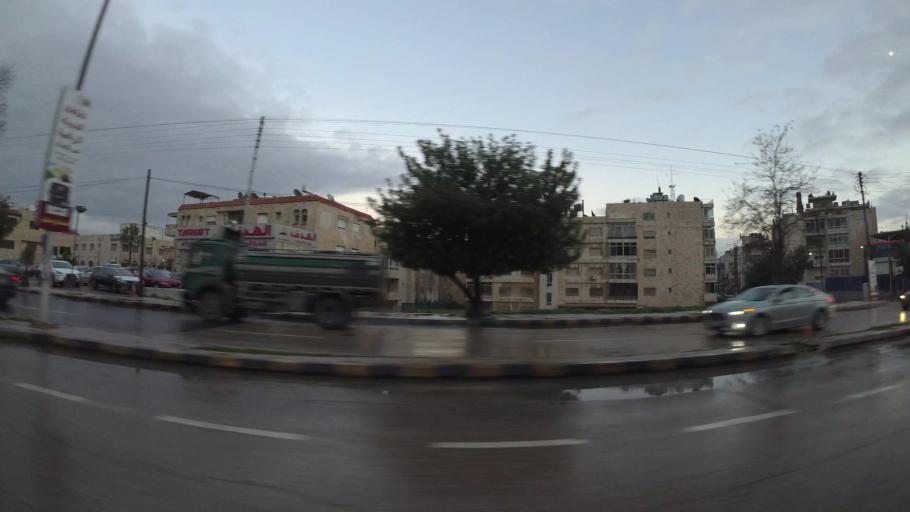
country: JO
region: Amman
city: Al Jubayhah
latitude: 31.9776
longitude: 35.8890
